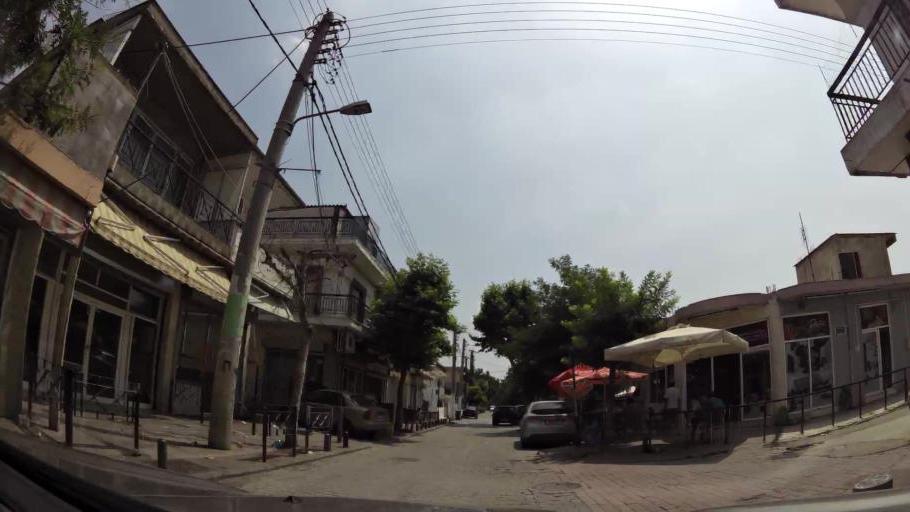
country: GR
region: Central Macedonia
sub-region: Nomos Thessalonikis
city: Menemeni
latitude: 40.6580
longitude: 22.8971
